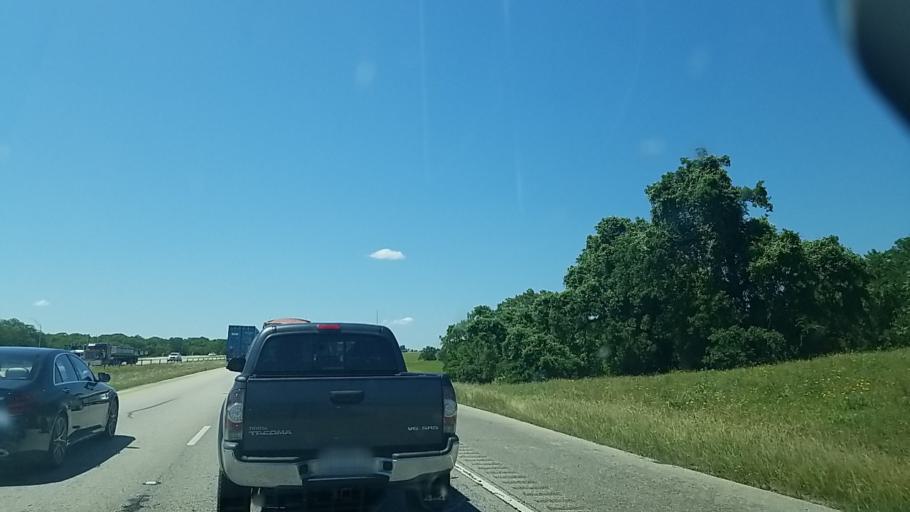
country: US
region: Texas
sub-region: Leon County
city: Buffalo
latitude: 31.4575
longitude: -96.0817
